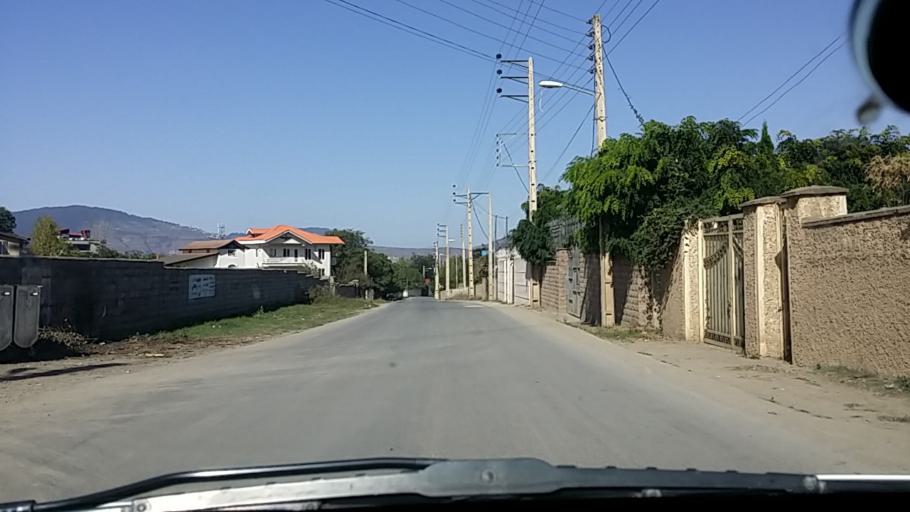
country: IR
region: Mazandaran
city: `Abbasabad
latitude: 36.5004
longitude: 51.1577
